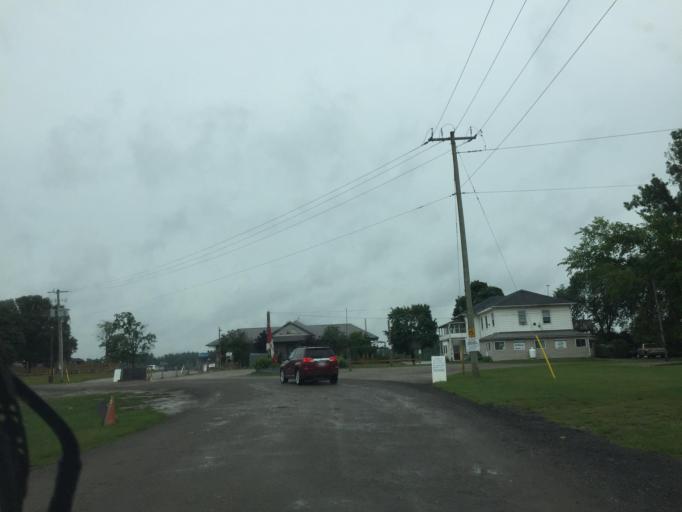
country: CA
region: Ontario
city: Cambridge
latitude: 43.4227
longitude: -80.2627
